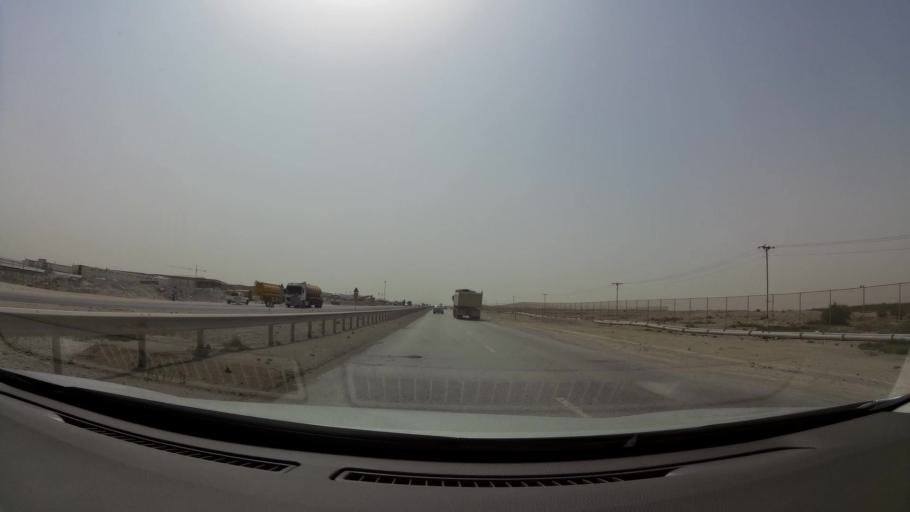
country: QA
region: Baladiyat ar Rayyan
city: Ar Rayyan
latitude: 25.2235
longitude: 51.3707
